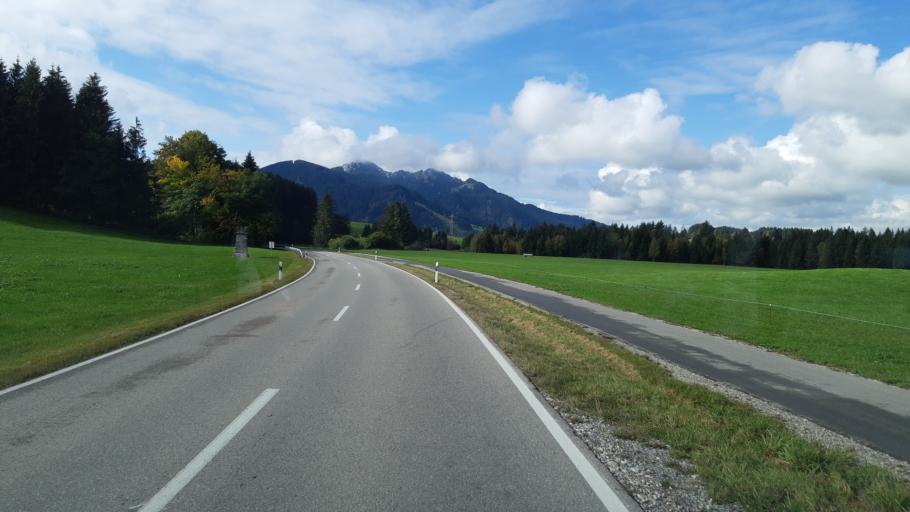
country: DE
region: Bavaria
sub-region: Swabia
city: Eisenberg
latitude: 47.6027
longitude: 10.5855
